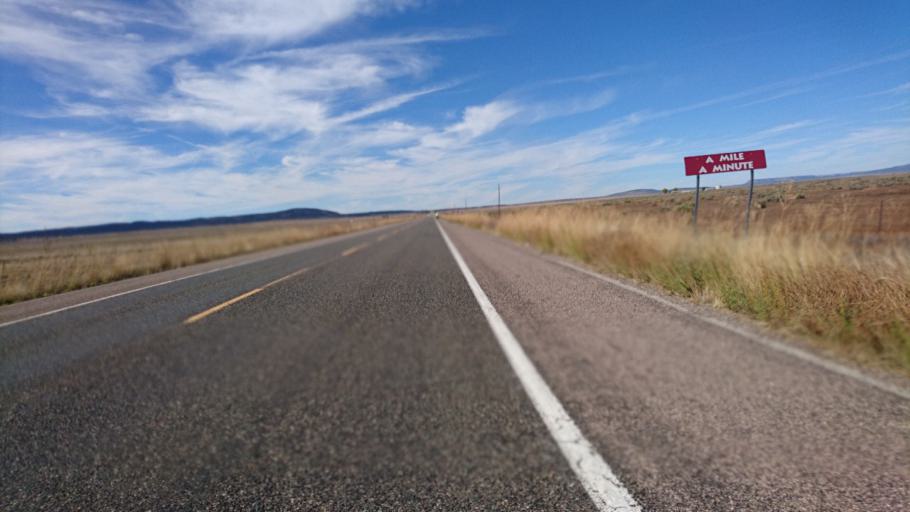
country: US
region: Arizona
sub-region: Mohave County
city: Peach Springs
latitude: 35.4610
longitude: -113.1104
